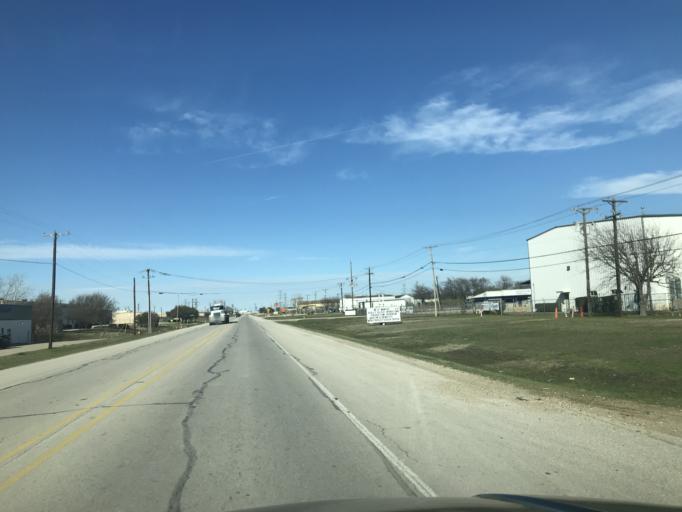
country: US
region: Texas
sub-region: Tarrant County
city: Blue Mound
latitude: 32.8308
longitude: -97.3429
